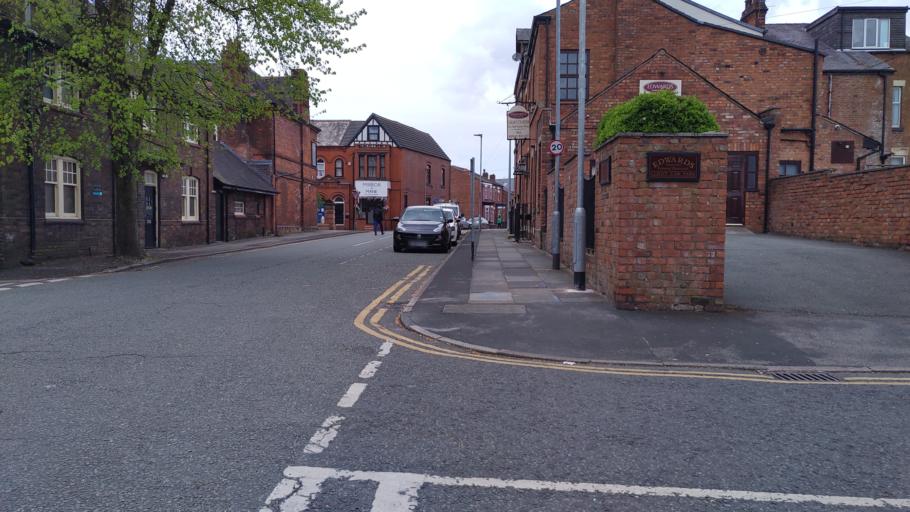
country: GB
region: England
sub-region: Borough of Wigan
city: Ince-in-Makerfield
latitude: 53.5505
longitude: -2.6298
